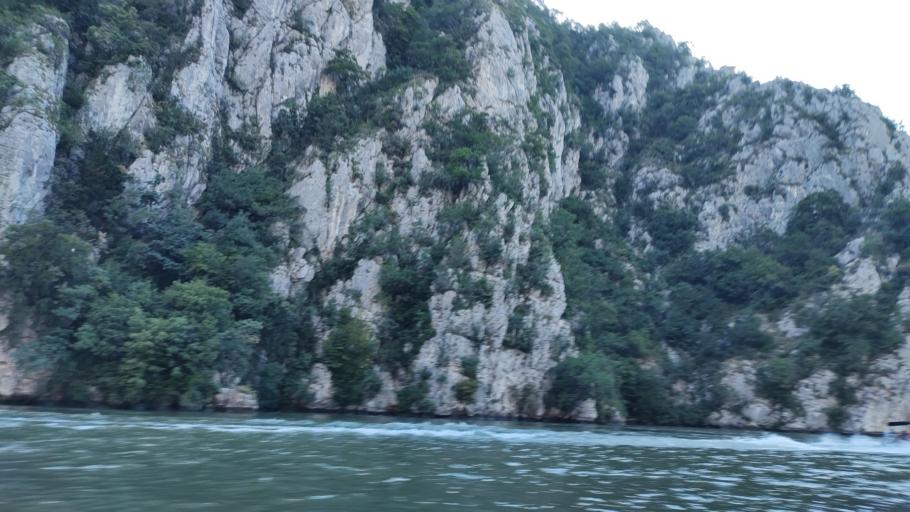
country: RO
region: Mehedinti
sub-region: Comuna Dubova
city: Dubova
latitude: 44.6150
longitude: 22.2727
